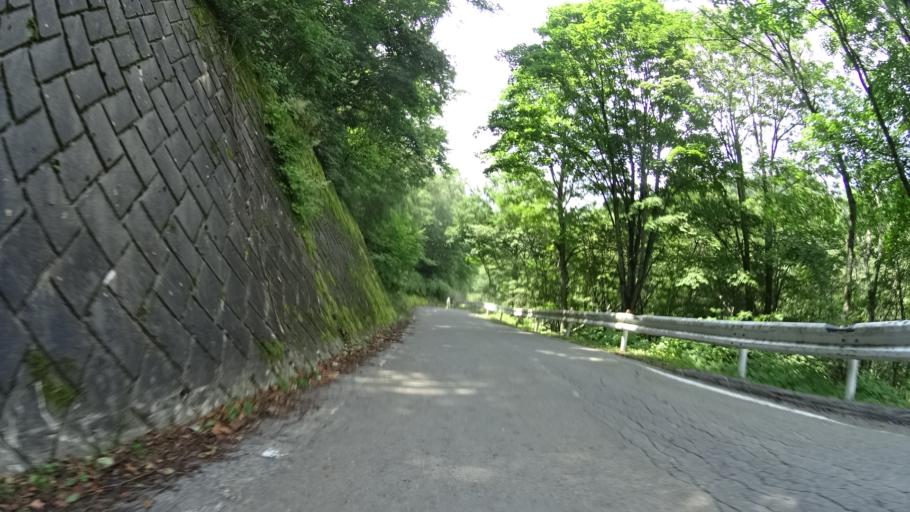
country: JP
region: Nagano
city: Saku
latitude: 36.1025
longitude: 138.6484
